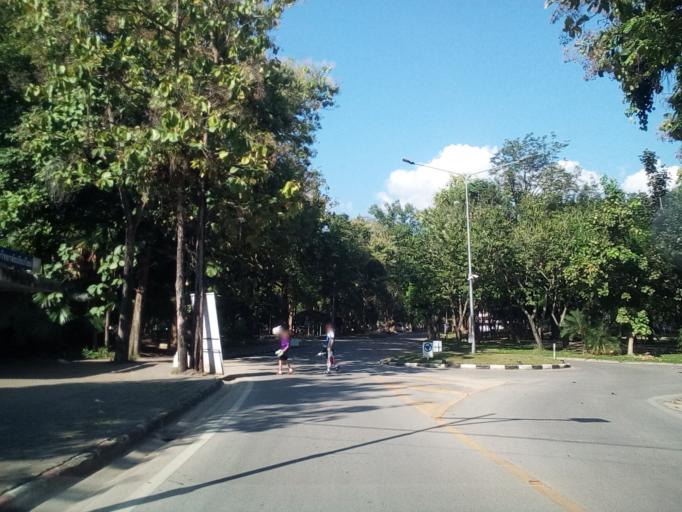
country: TH
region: Chiang Mai
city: Chiang Mai
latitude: 18.7995
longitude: 98.9560
